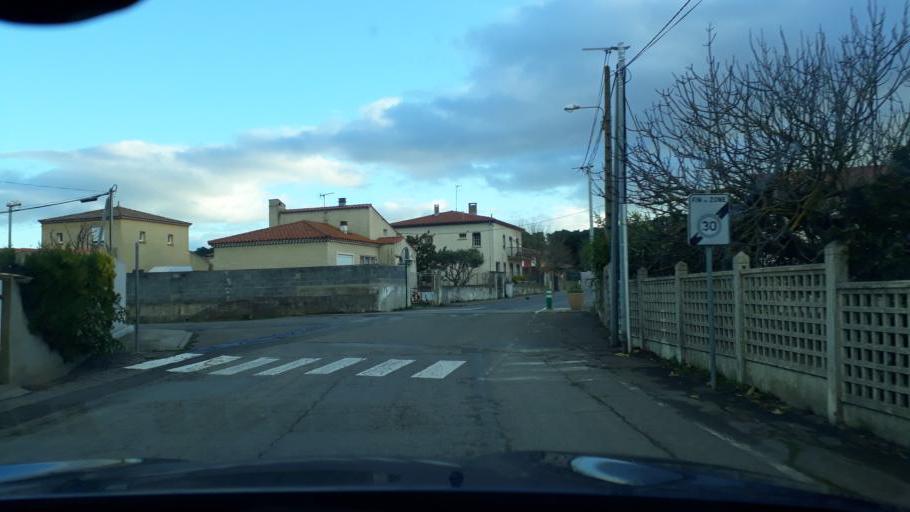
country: FR
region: Languedoc-Roussillon
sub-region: Departement de l'Herault
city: Nissan-lez-Enserune
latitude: 43.2866
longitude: 3.1321
